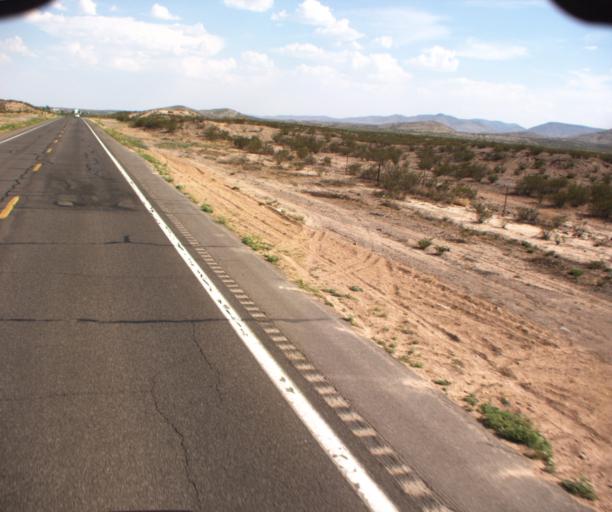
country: US
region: Arizona
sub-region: Greenlee County
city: Clifton
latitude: 32.7780
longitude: -109.1563
